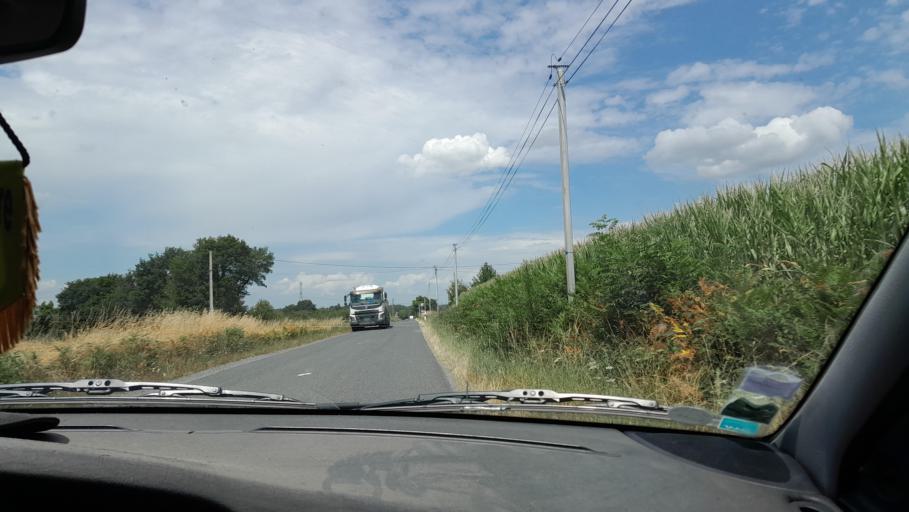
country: FR
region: Pays de la Loire
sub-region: Departement de la Mayenne
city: Saint-Pierre-la-Cour
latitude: 48.1402
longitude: -1.0273
